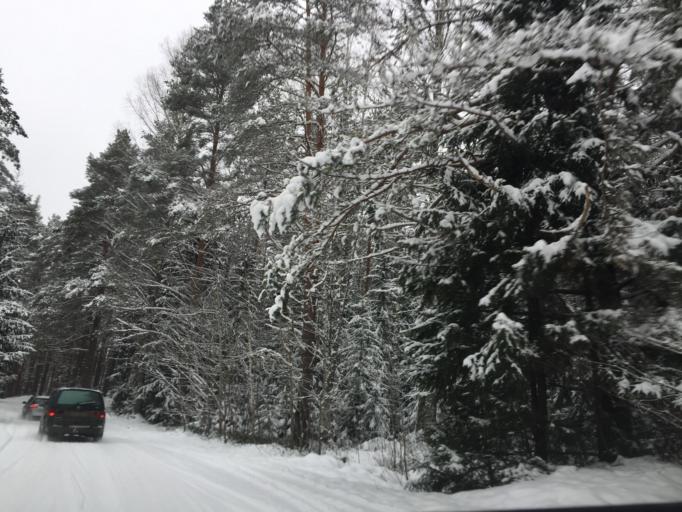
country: LV
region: Smiltene
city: Smiltene
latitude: 57.4017
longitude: 25.9493
